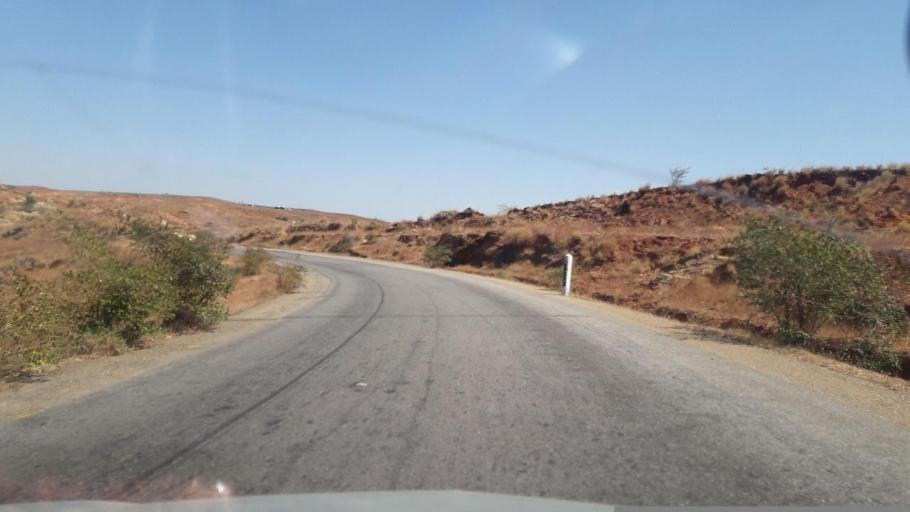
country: MG
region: Betsiboka
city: Maevatanana
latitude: -16.9441
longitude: 46.8552
